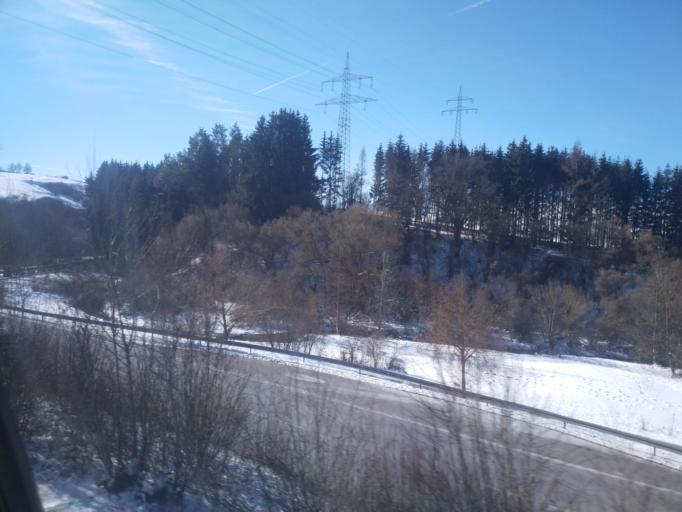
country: DE
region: Baden-Wuerttemberg
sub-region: Freiburg Region
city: Aldingen
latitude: 48.1036
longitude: 8.6994
